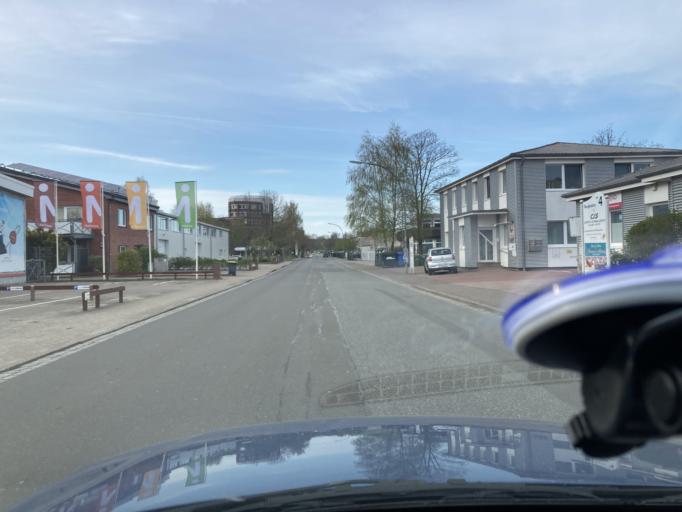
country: DE
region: Schleswig-Holstein
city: Heide
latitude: 54.2061
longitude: 9.0993
